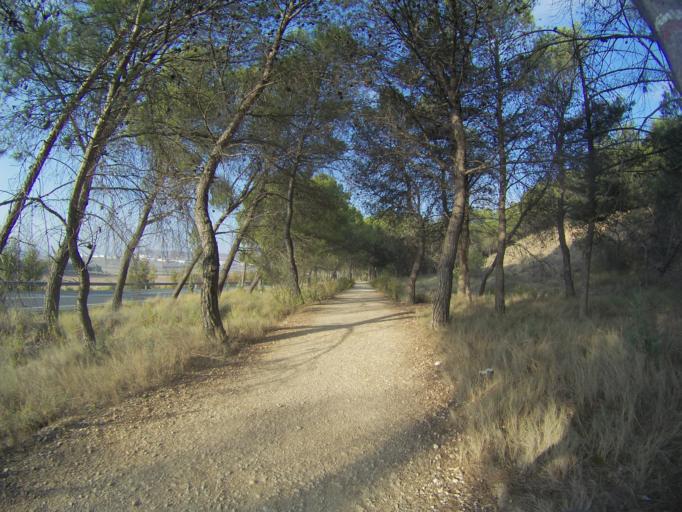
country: ES
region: Basque Country
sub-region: Provincia de Alava
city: Oyon
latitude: 42.4930
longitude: -2.4072
